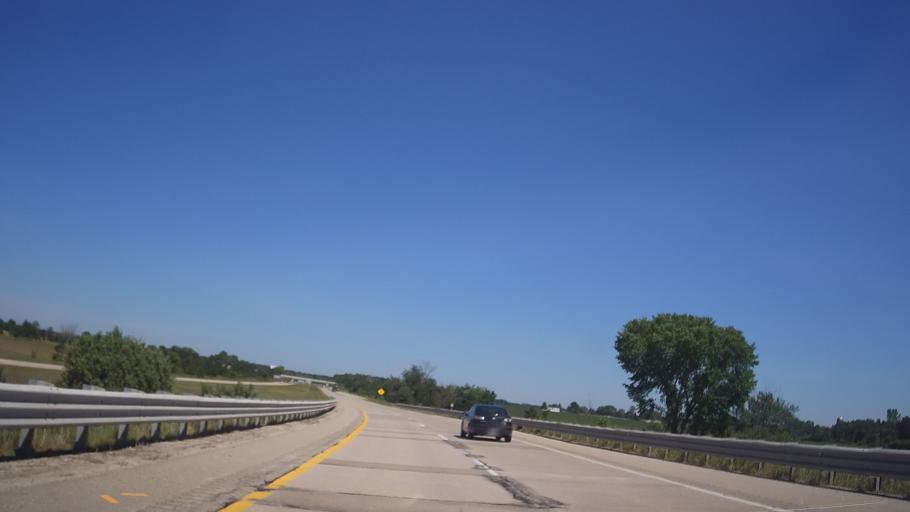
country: US
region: Michigan
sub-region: Clare County
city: Clare
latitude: 43.8082
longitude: -84.7201
